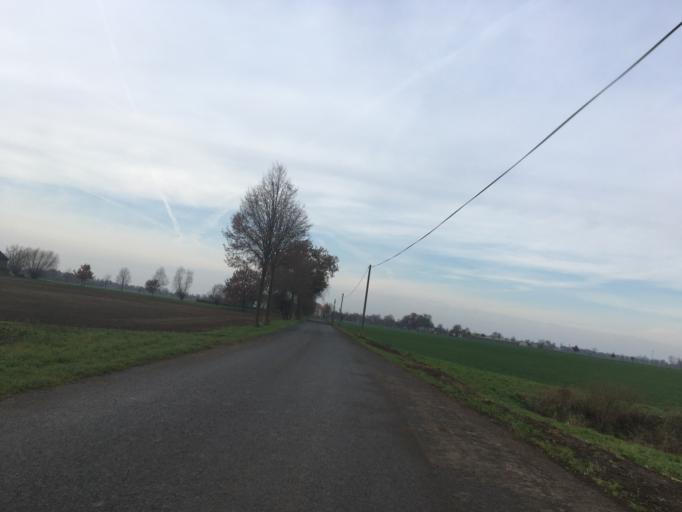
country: DE
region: Brandenburg
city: Neulewin
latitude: 52.7105
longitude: 14.3260
